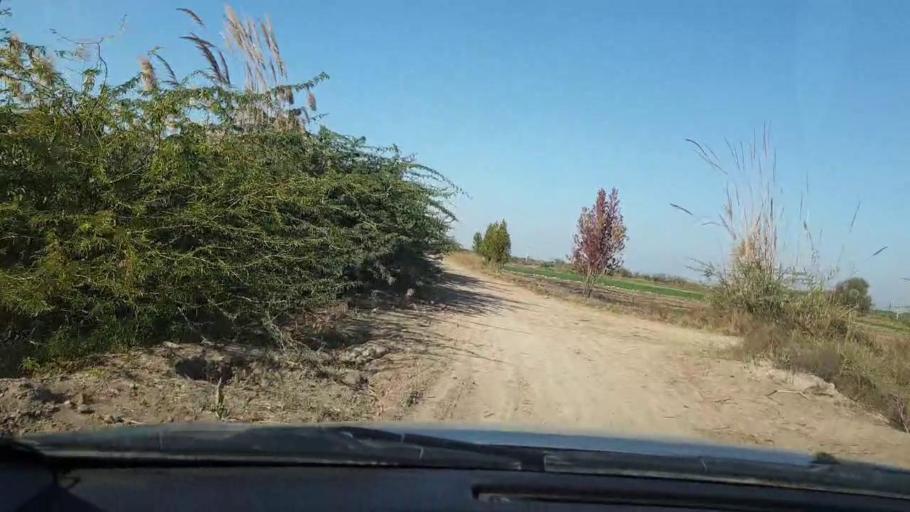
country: PK
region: Sindh
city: Berani
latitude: 25.7340
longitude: 68.9832
